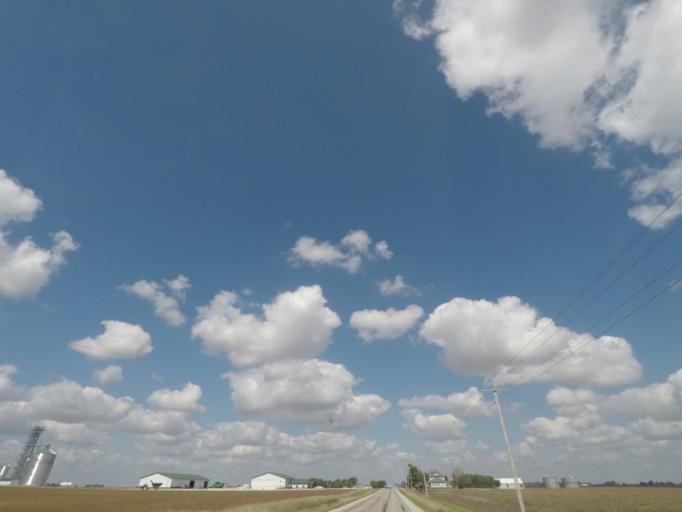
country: US
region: Iowa
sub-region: Story County
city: Nevada
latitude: 42.0469
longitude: -93.4057
